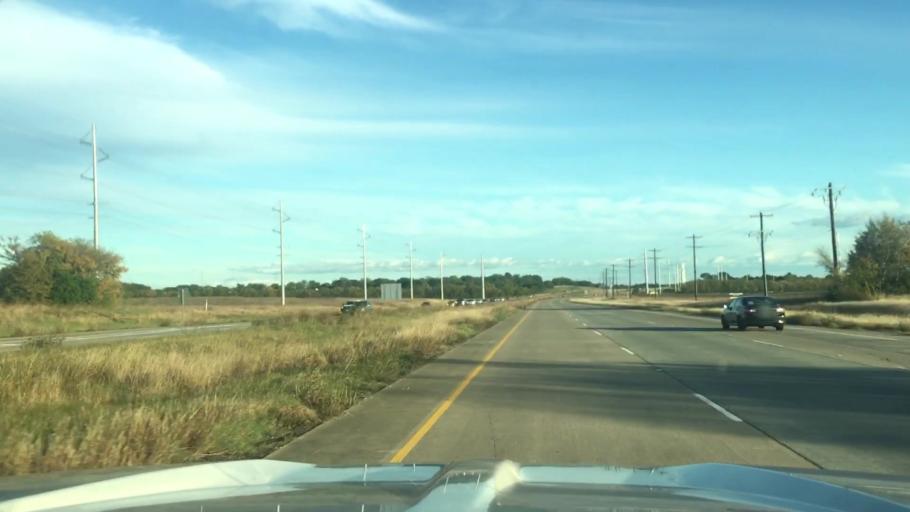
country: US
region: Texas
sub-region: Denton County
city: Denton
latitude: 33.2558
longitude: -97.1058
